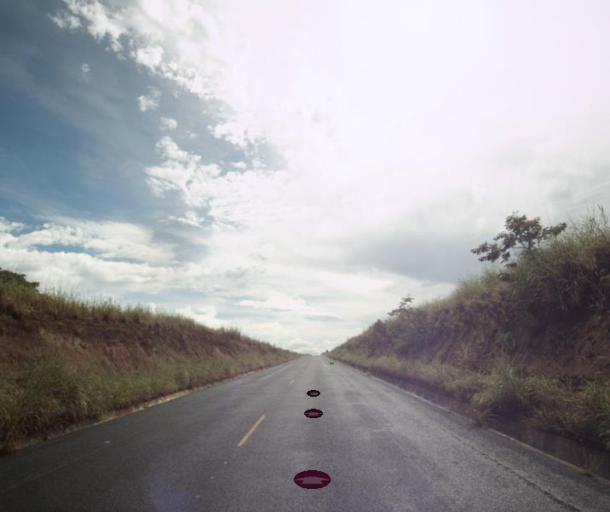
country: BR
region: Goias
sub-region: Sao Miguel Do Araguaia
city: Sao Miguel do Araguaia
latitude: -13.2966
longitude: -50.3480
